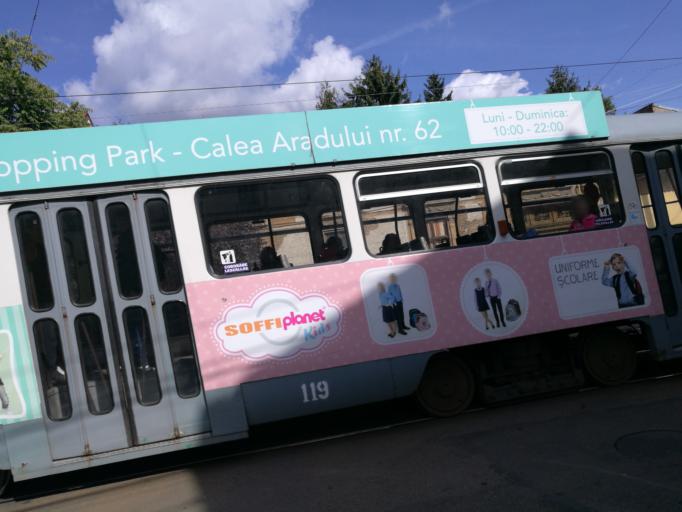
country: RO
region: Bihor
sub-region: Comuna Biharea
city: Oradea
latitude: 47.0566
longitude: 21.9238
